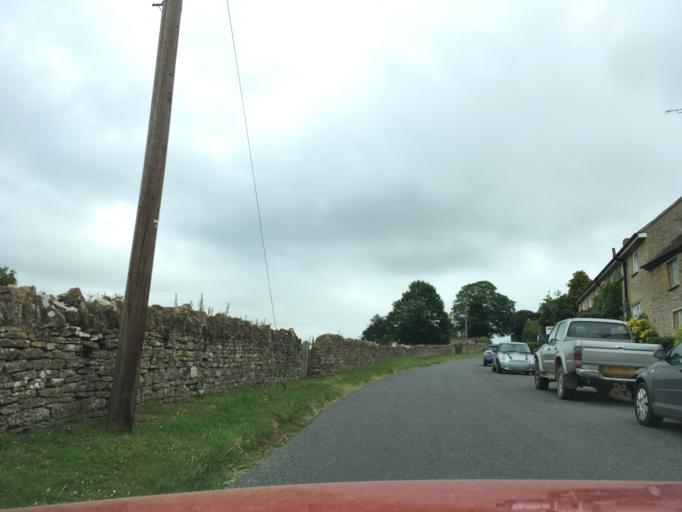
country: GB
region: England
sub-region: Oxfordshire
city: Somerton
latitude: 51.9966
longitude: -1.2545
